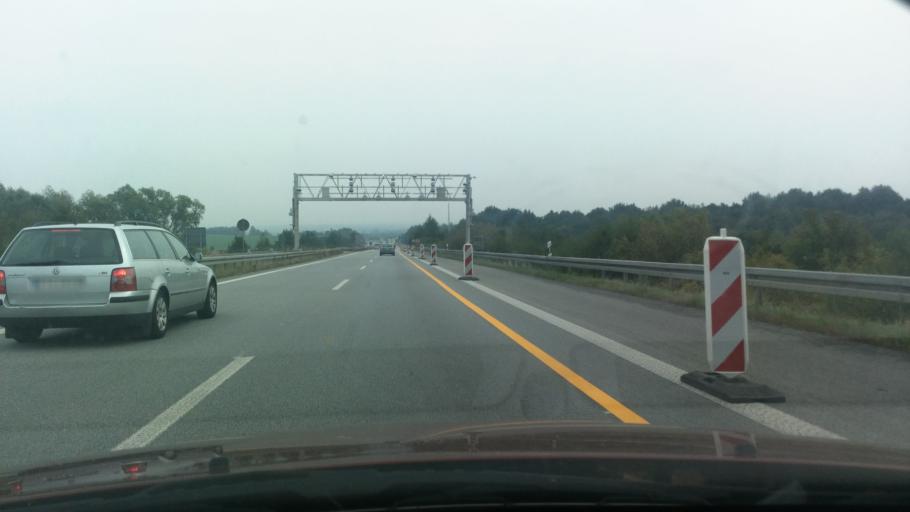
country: DE
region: Saxony
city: Goerlitz
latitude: 51.1925
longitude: 14.9751
